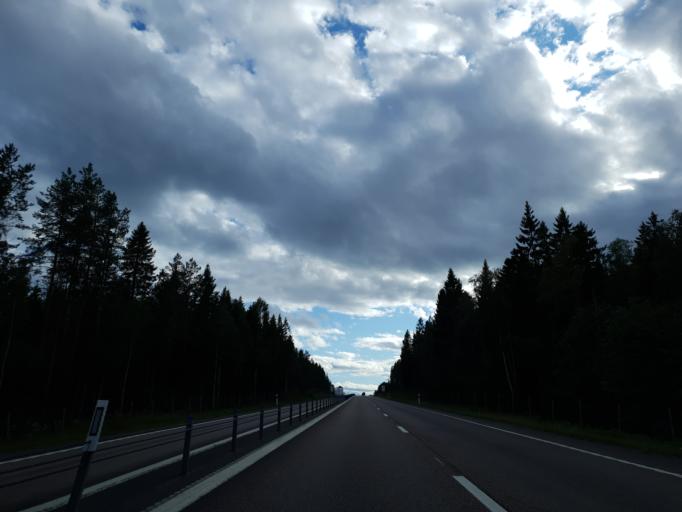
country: SE
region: Vaesternorrland
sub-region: Haernoesands Kommun
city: Haernoesand
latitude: 62.5732
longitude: 17.7463
